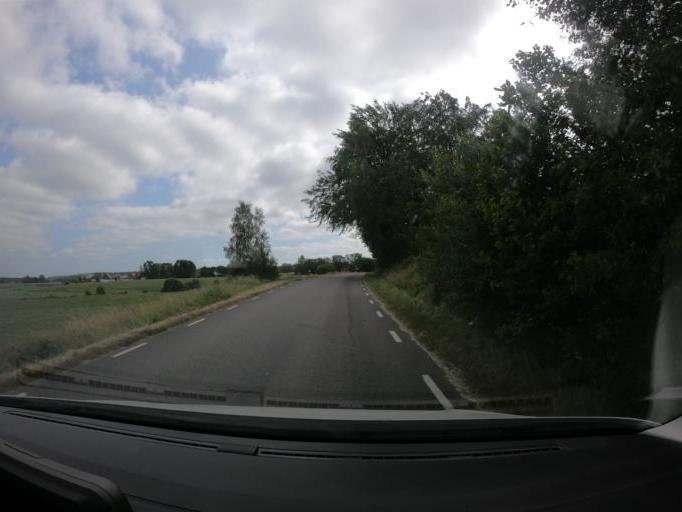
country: SE
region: Skane
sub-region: Hassleholms Kommun
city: Tormestorp
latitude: 56.1506
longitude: 13.6293
